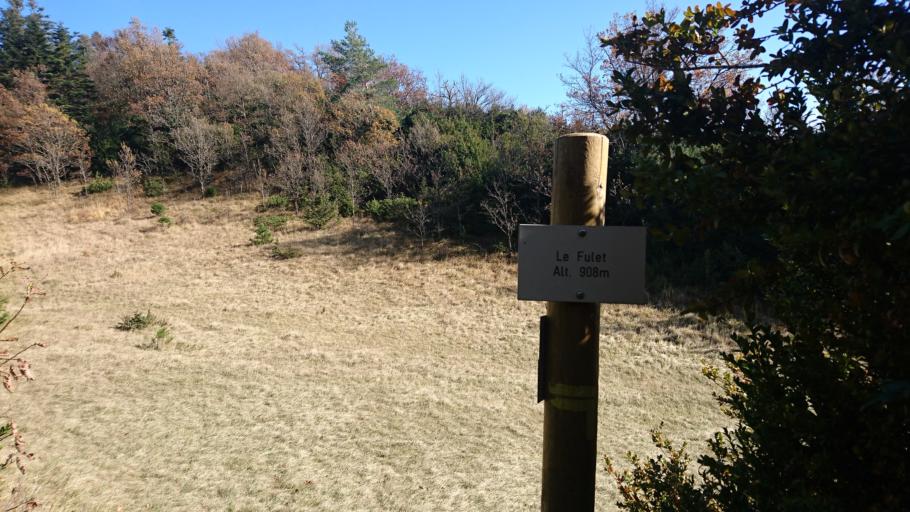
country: FR
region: Rhone-Alpes
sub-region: Departement de l'Ain
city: Nantua
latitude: 46.1572
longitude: 5.6172
